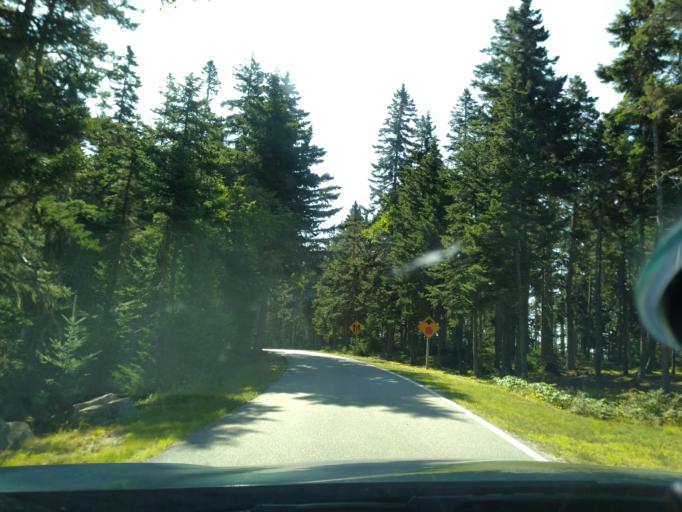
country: US
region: Maine
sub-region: Hancock County
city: Gouldsboro
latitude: 44.3389
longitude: -68.0563
